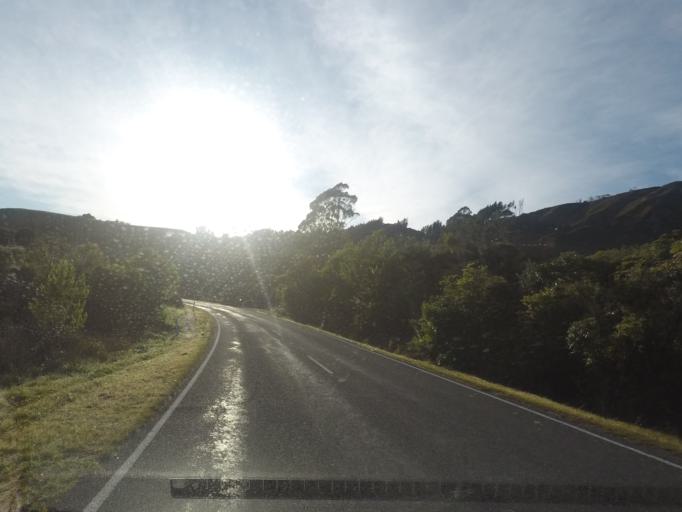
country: NZ
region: Tasman
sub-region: Tasman District
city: Takaka
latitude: -40.8182
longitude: 172.9146
